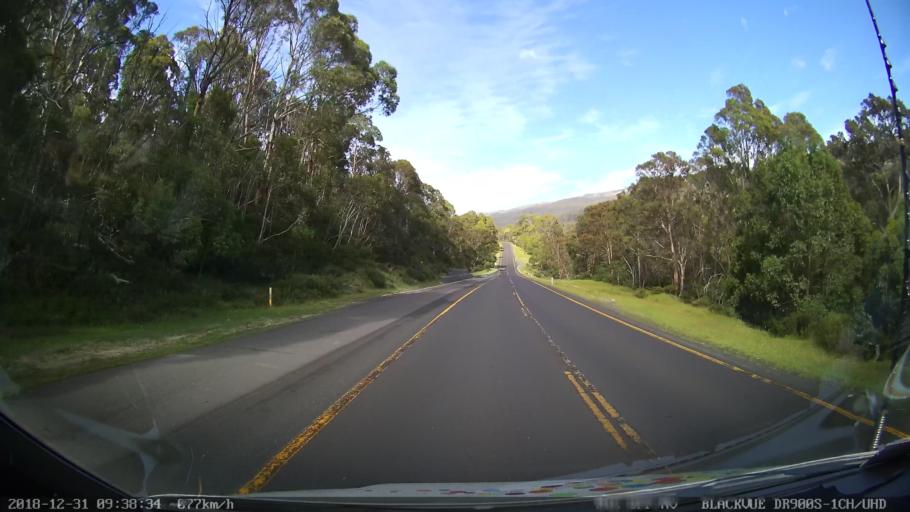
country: AU
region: New South Wales
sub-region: Snowy River
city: Jindabyne
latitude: -36.4750
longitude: 148.3661
